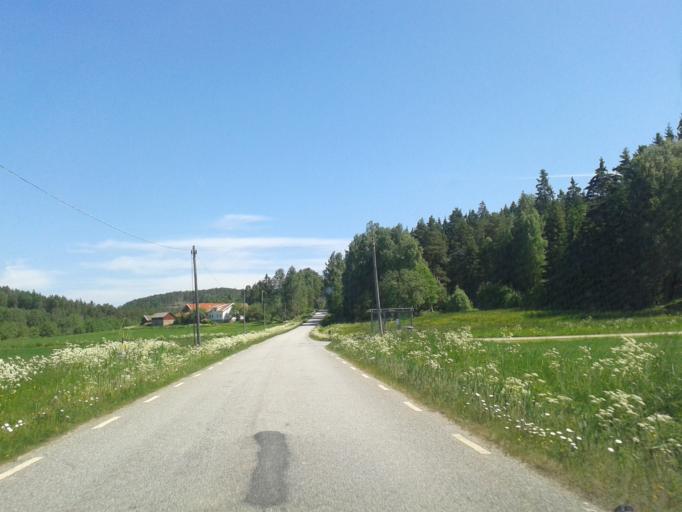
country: SE
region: Vaestra Goetaland
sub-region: Stromstads Kommun
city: Stroemstad
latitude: 58.8952
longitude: 11.3132
